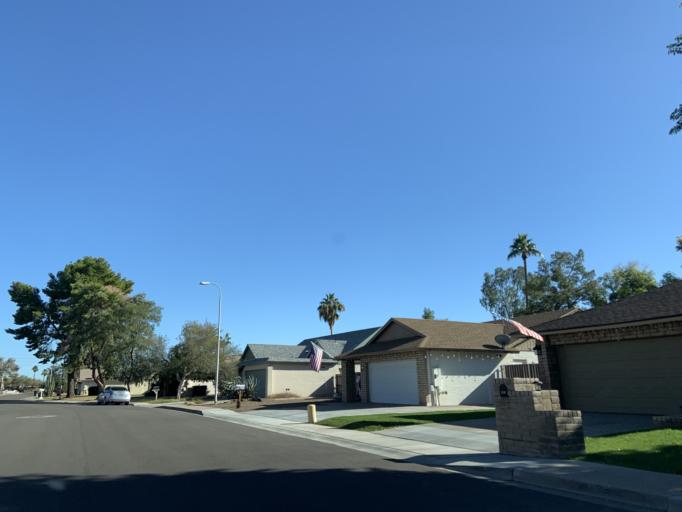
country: US
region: Arizona
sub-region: Maricopa County
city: San Carlos
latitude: 33.3542
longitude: -111.8795
